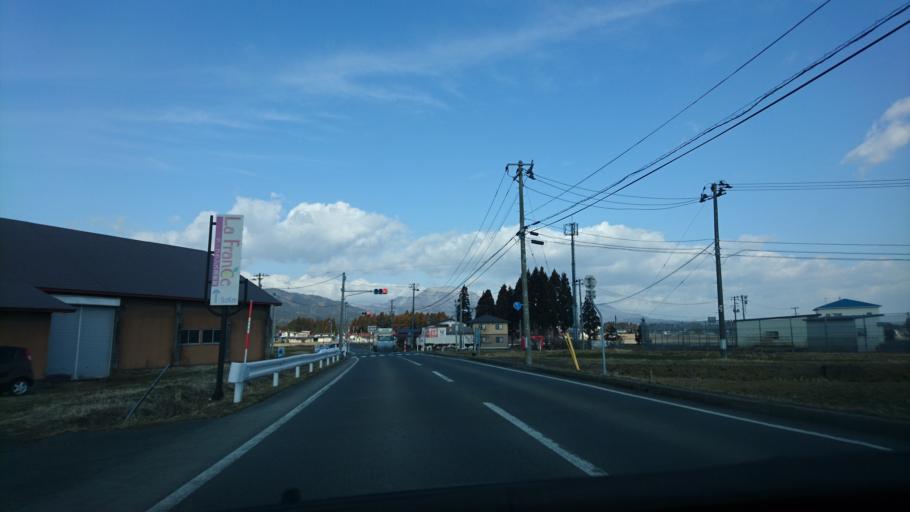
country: JP
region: Iwate
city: Hanamaki
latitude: 39.5202
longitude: 141.1280
